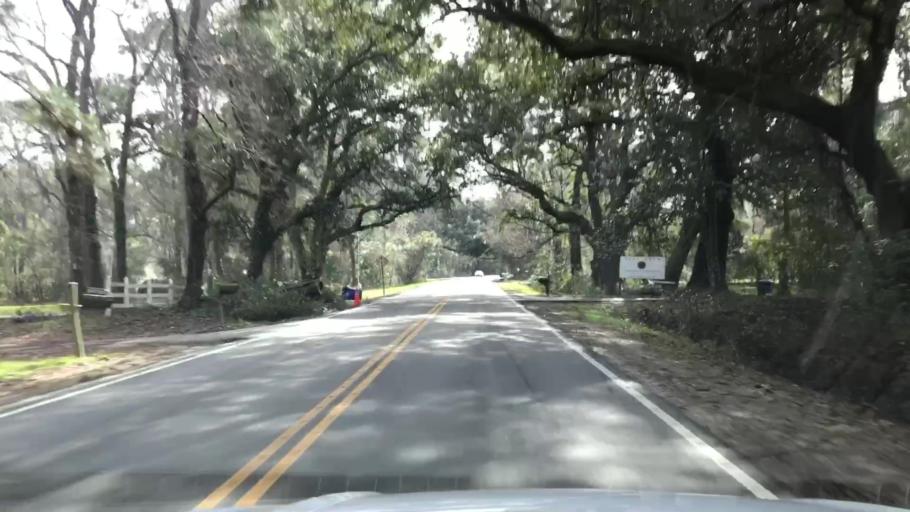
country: US
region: South Carolina
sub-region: Charleston County
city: Shell Point
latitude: 32.7276
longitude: -80.0250
